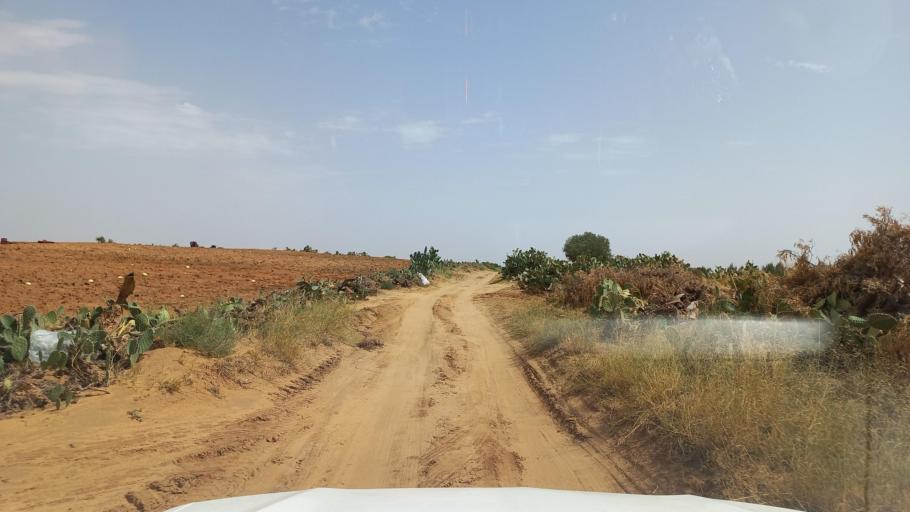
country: TN
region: Al Qasrayn
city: Kasserine
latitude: 35.2478
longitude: 9.0638
